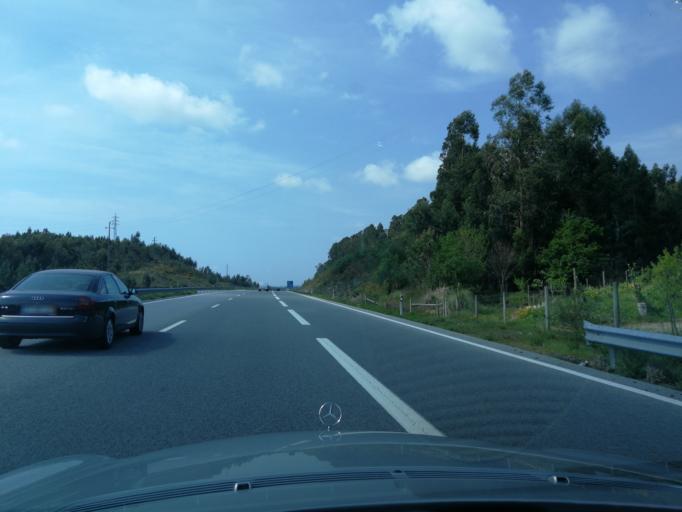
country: PT
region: Braga
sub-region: Vila Nova de Famalicao
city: Ribeirao
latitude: 41.3802
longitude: -8.5732
